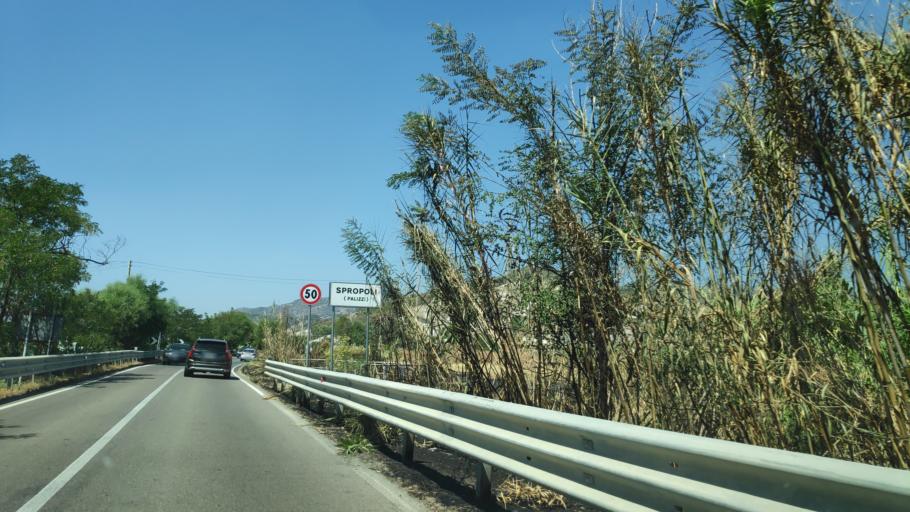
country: IT
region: Calabria
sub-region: Provincia di Reggio Calabria
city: Palizzi Marina
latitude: 37.9232
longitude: 16.0436
